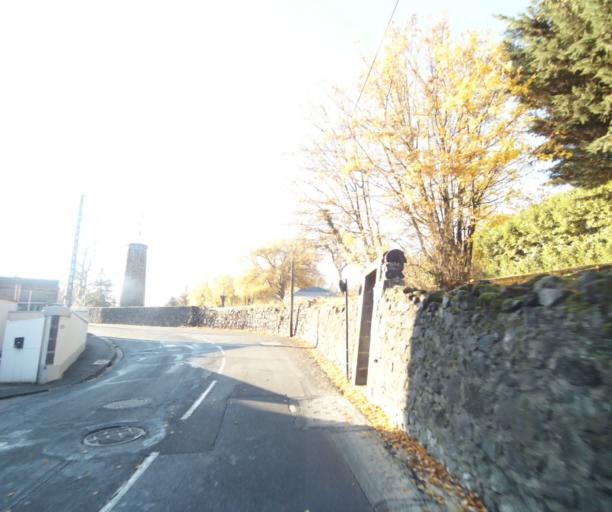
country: FR
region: Auvergne
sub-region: Departement du Puy-de-Dome
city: Nohanent
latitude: 45.8074
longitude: 3.0556
